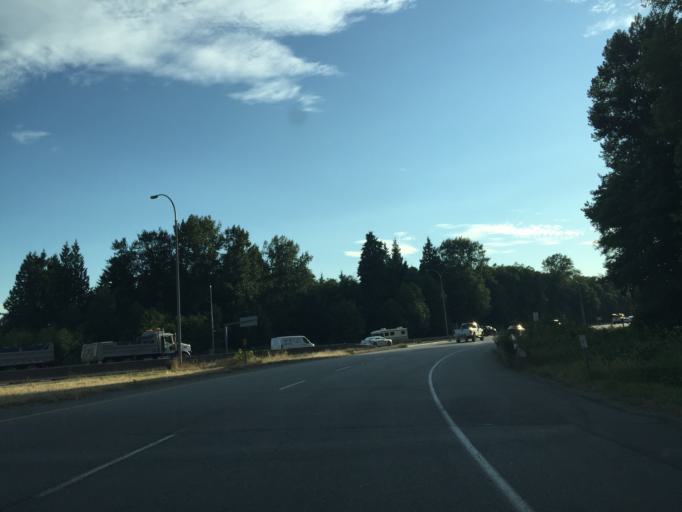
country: CA
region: British Columbia
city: Walnut Grove
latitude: 49.1655
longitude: -122.6715
